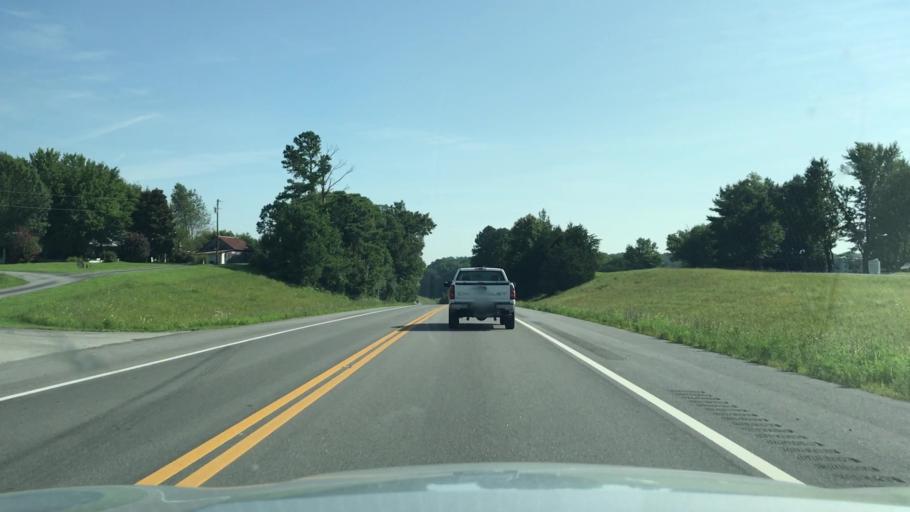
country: US
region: Tennessee
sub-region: Pickett County
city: Byrdstown
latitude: 36.4855
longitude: -85.1847
